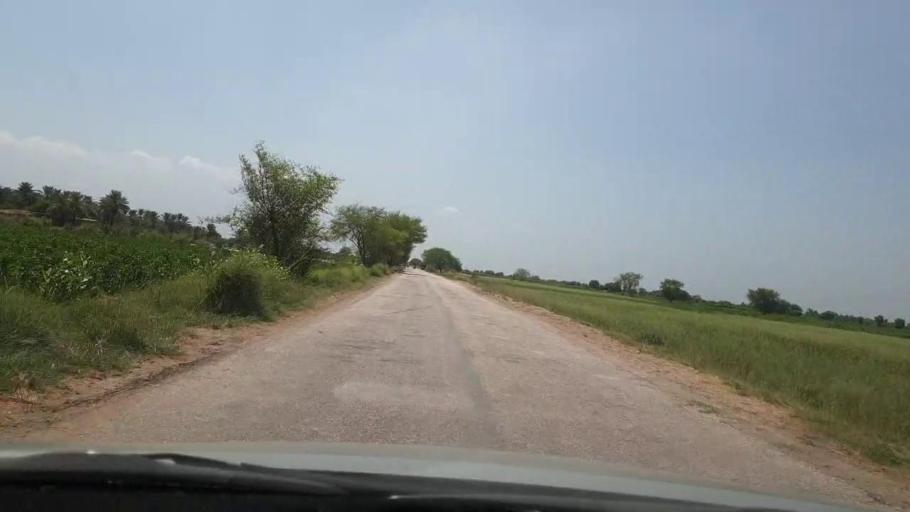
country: PK
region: Sindh
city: Pano Aqil
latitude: 27.6635
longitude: 69.1271
